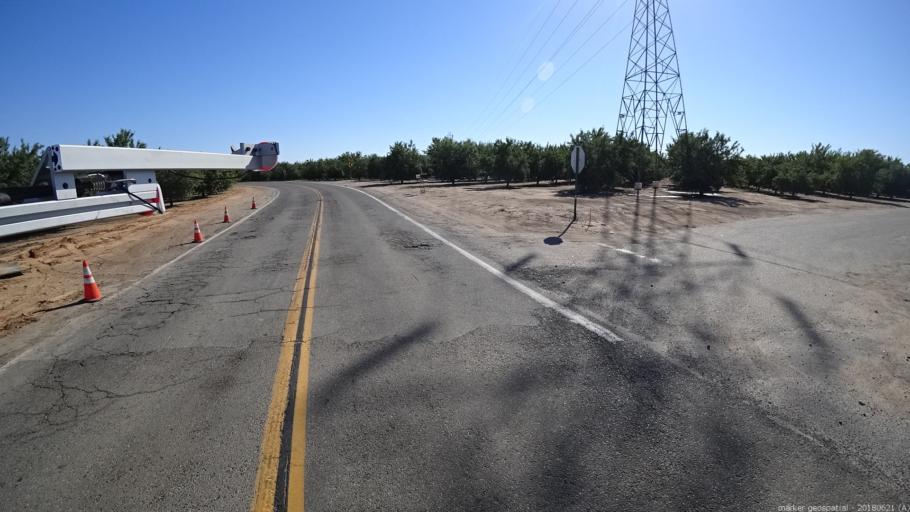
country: US
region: California
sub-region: Fresno County
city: Biola
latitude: 36.8525
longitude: -119.9094
